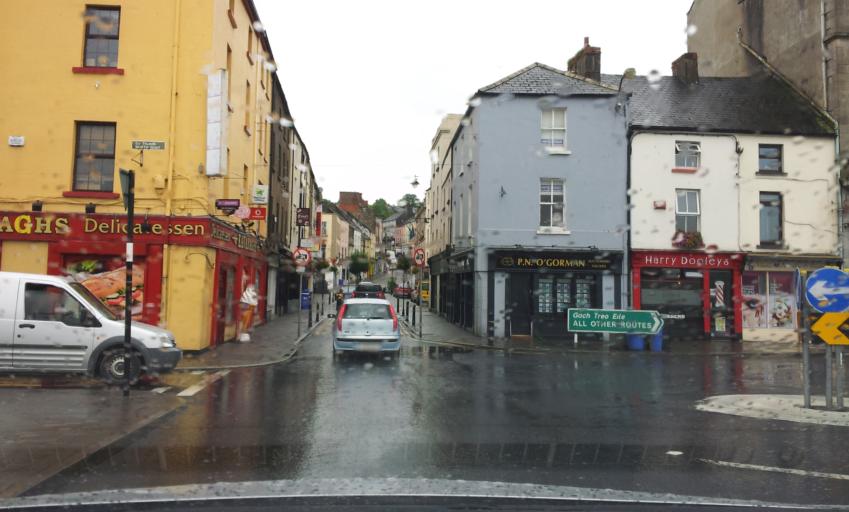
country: IE
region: Leinster
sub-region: Loch Garman
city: New Ross
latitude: 52.3959
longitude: -6.9456
